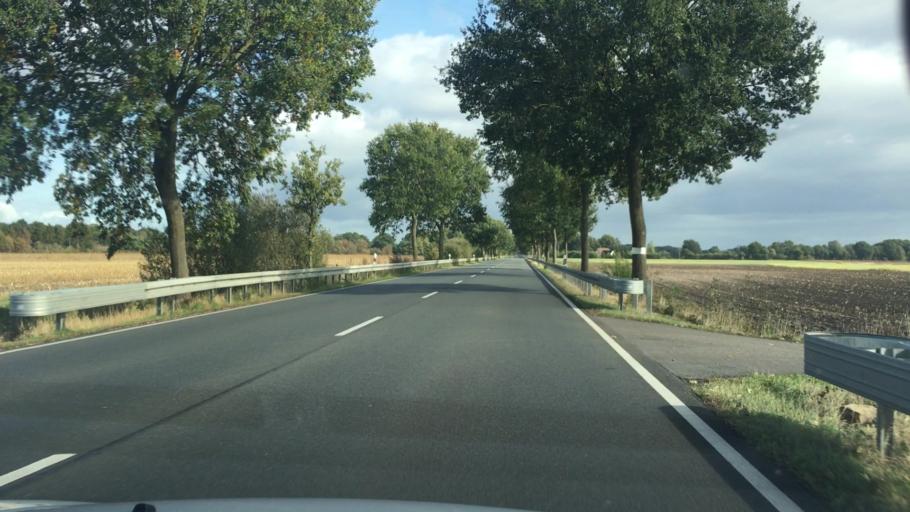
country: DE
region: Lower Saxony
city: Barver
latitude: 52.6102
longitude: 8.5570
